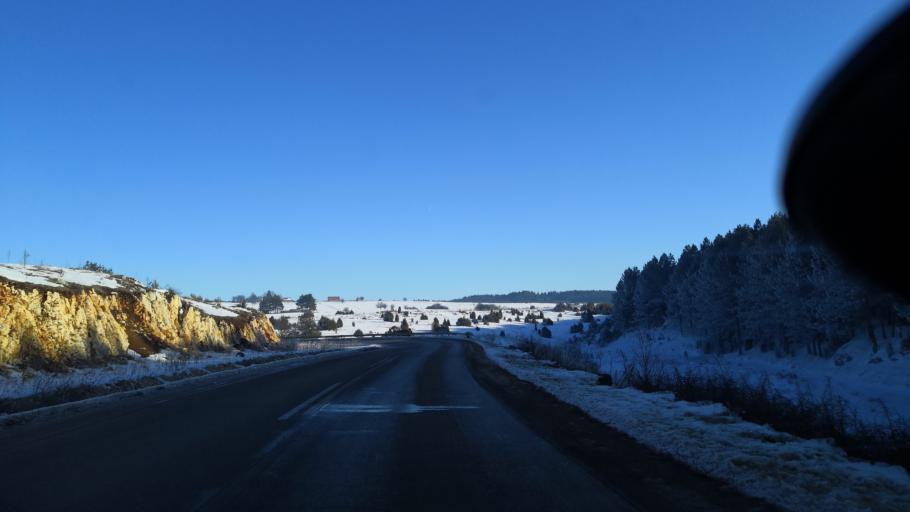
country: BA
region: Republika Srpska
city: Sokolac
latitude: 43.9351
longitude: 18.8182
